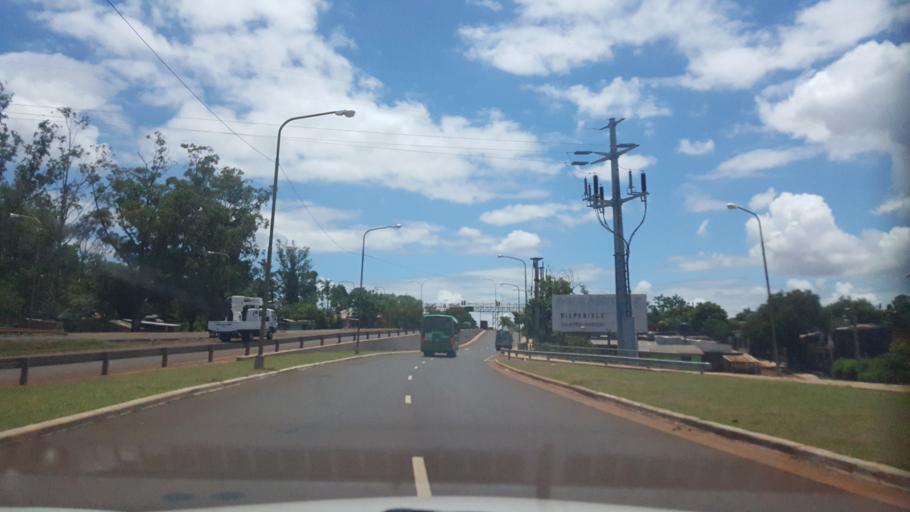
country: AR
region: Misiones
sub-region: Departamento de Capital
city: Posadas
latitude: -27.4178
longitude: -55.9000
